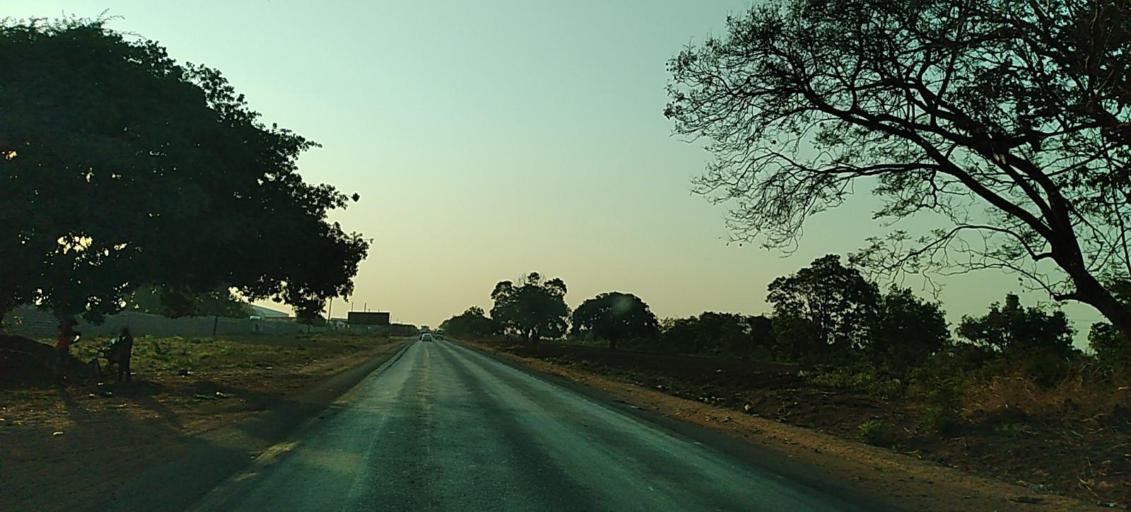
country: ZM
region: Copperbelt
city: Ndola
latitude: -13.0245
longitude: 28.6755
